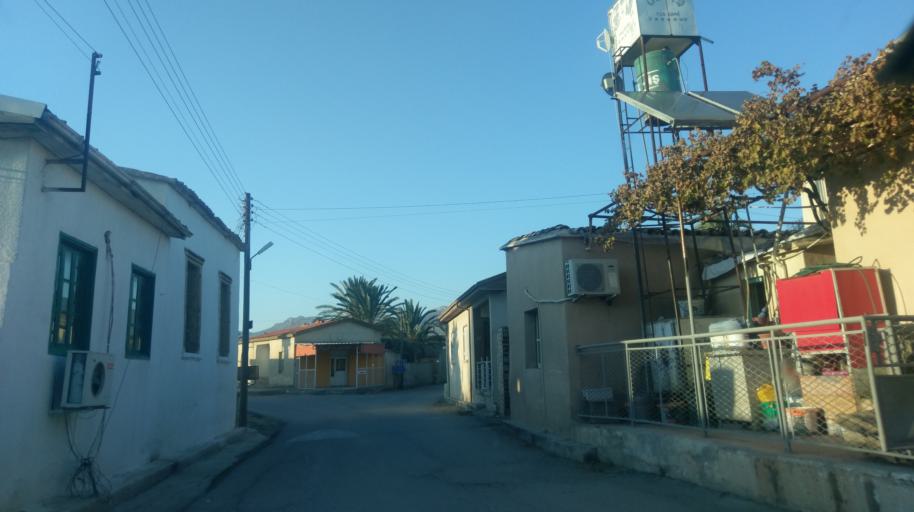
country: CY
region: Lefkosia
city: Geri
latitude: 35.2282
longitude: 33.5125
